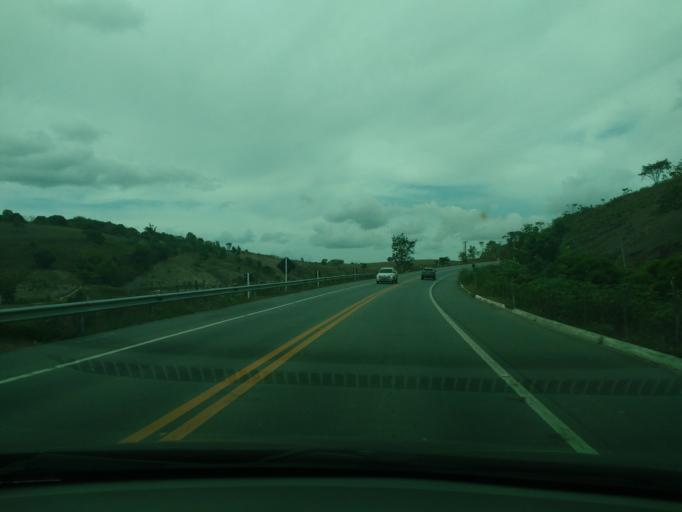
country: BR
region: Alagoas
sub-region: Murici
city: Murici
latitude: -9.2452
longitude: -36.0034
